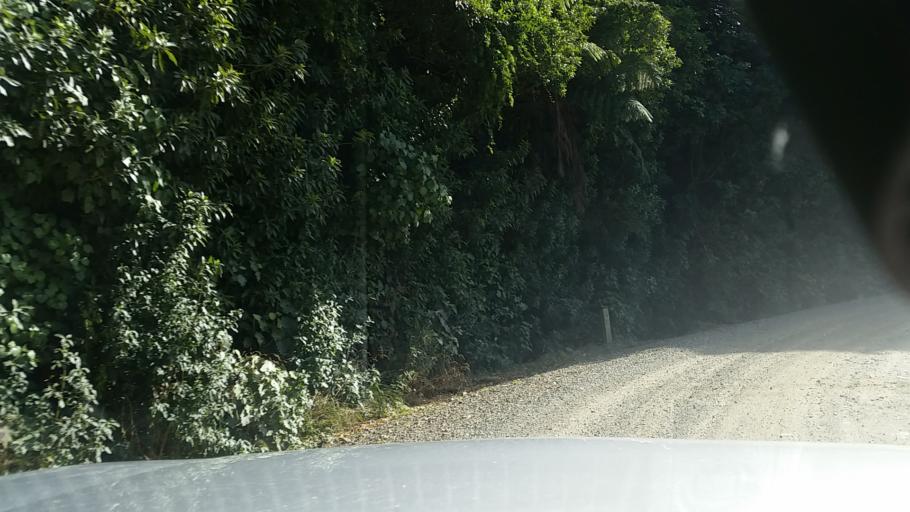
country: NZ
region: Marlborough
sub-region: Marlborough District
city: Picton
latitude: -41.2951
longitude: 174.1238
